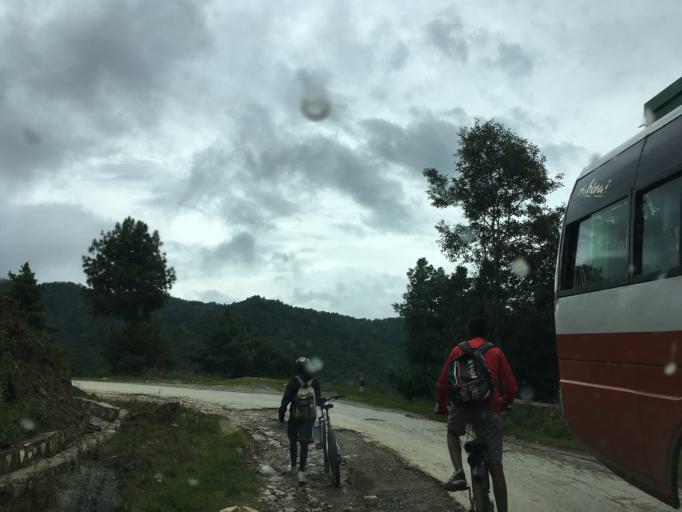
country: NP
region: Central Region
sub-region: Bagmati Zone
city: Nagarkot
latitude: 27.7101
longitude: 85.4992
